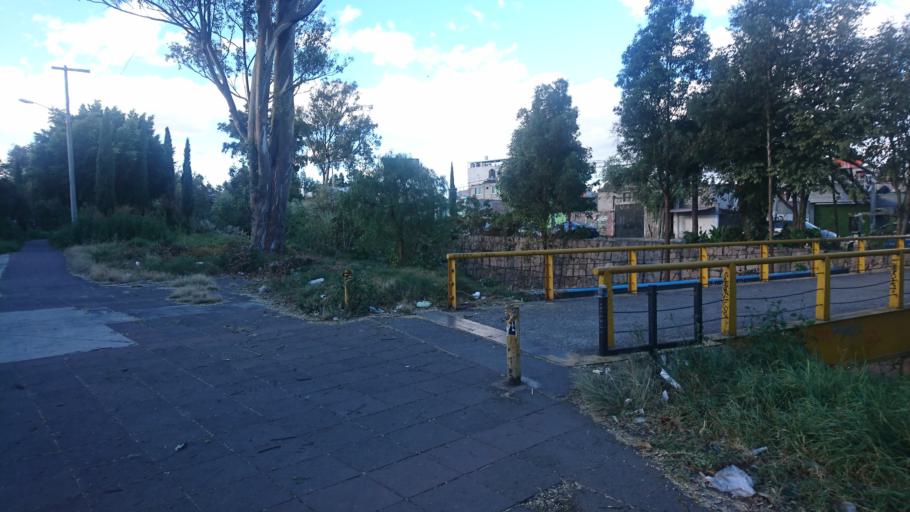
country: MX
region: Mexico City
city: Iztapalapa
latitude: 19.3266
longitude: -99.1061
